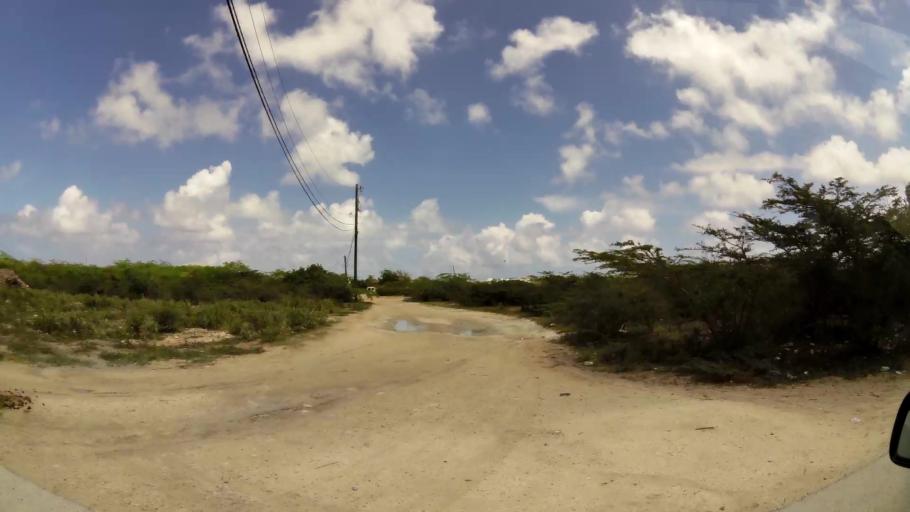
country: TC
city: Cockburn Town
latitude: 21.4601
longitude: -71.1394
